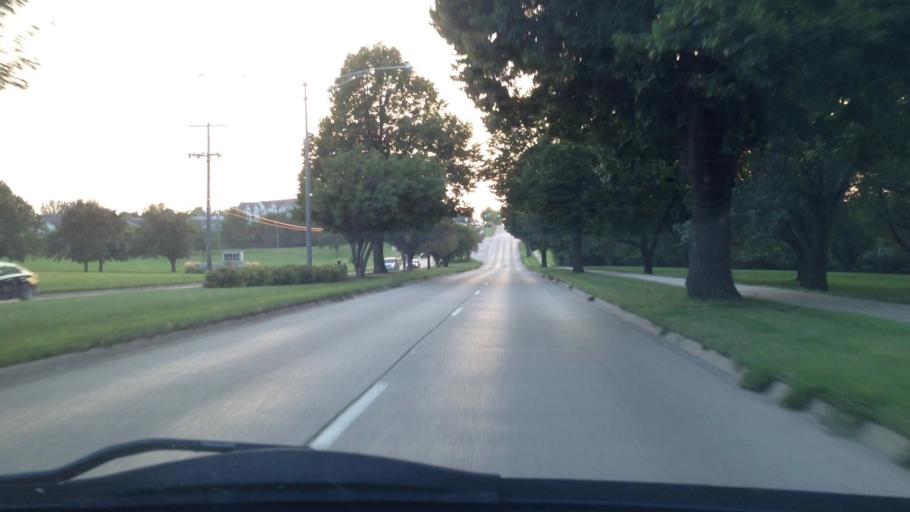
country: US
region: Iowa
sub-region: Johnson County
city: Coralville
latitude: 41.6571
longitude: -91.5799
